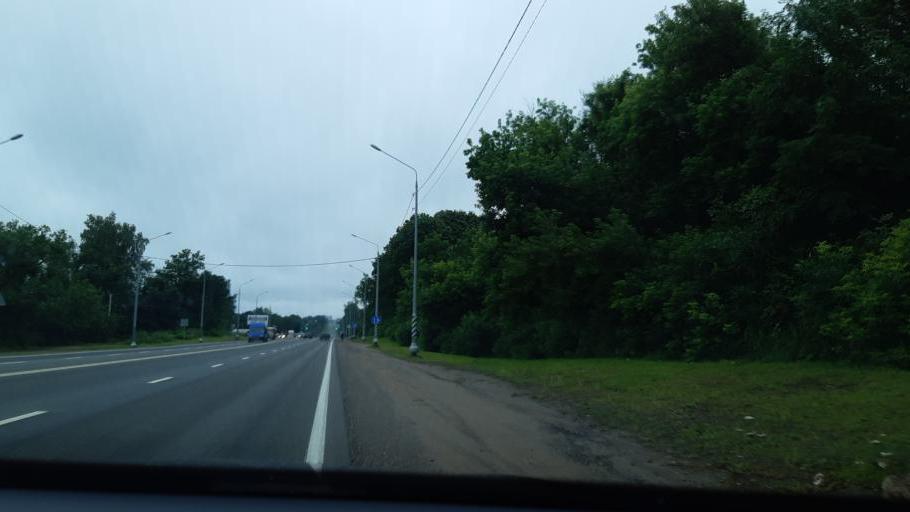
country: RU
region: Smolensk
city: Smolensk
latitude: 54.7170
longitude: 32.1074
